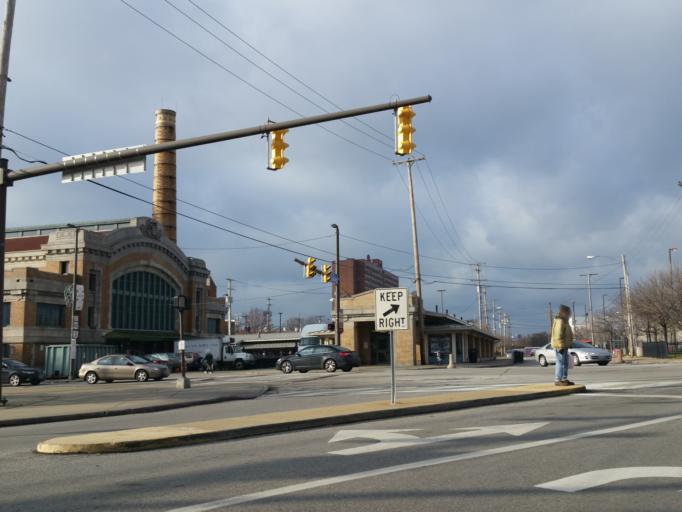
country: US
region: Ohio
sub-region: Cuyahoga County
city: Cleveland
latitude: 41.4845
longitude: -81.7018
